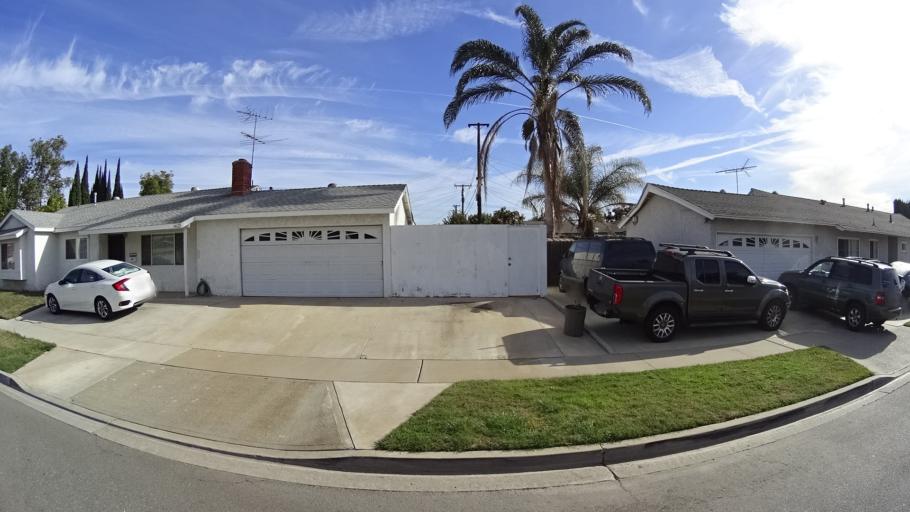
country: US
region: California
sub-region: Orange County
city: Garden Grove
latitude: 33.7500
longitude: -117.9436
